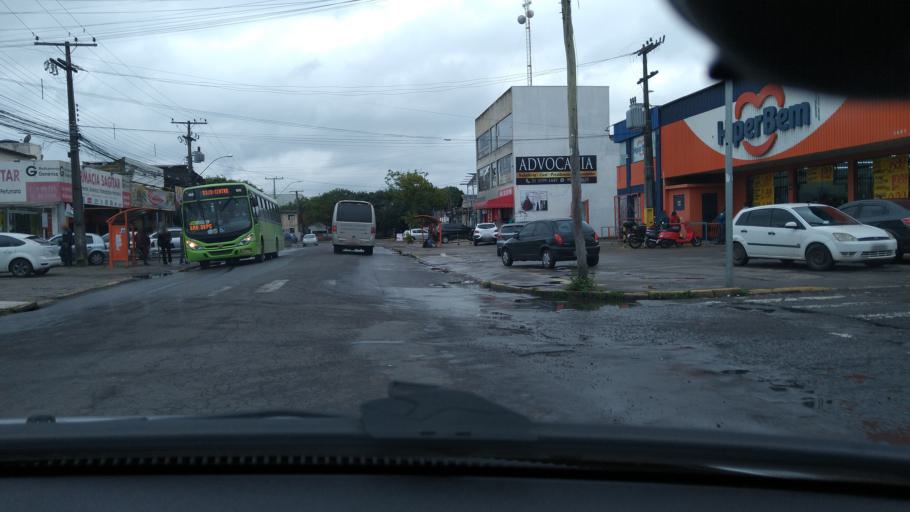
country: BR
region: Rio Grande do Sul
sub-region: Canoas
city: Canoas
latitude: -29.9011
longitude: -51.2204
